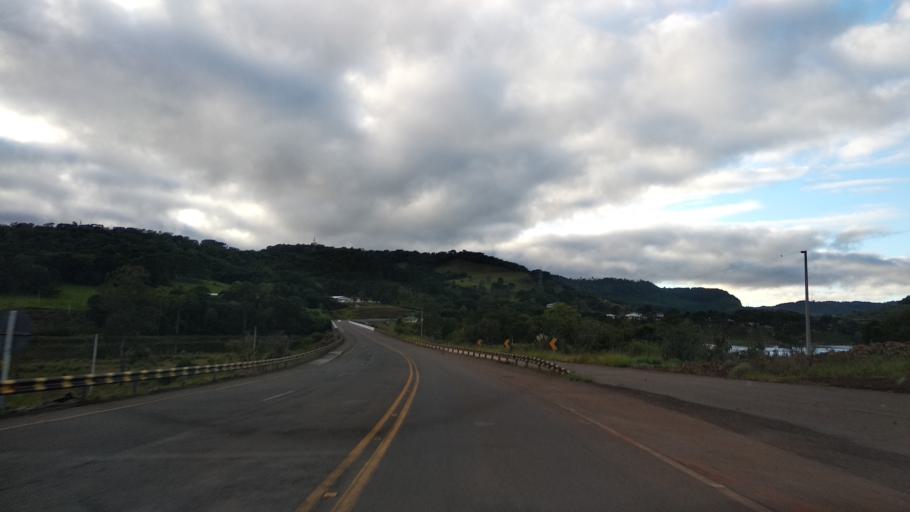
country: BR
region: Santa Catarina
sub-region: Curitibanos
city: Curitibanos
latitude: -27.5376
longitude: -50.8652
